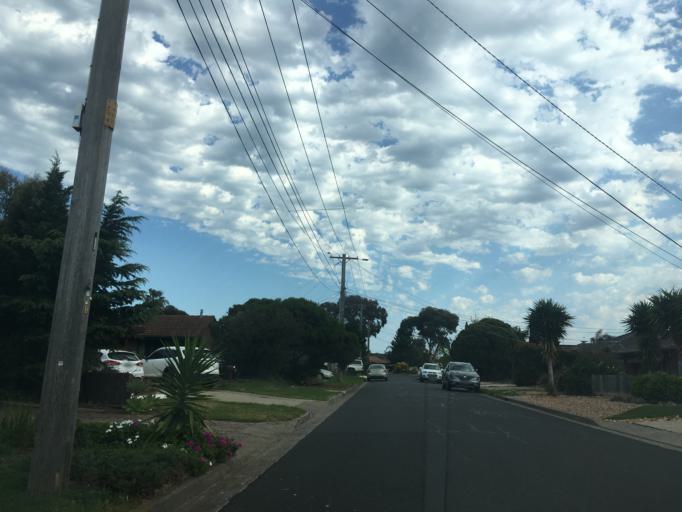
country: AU
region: Victoria
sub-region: Wyndham
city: Hoppers Crossing
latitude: -37.8631
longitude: 144.7088
